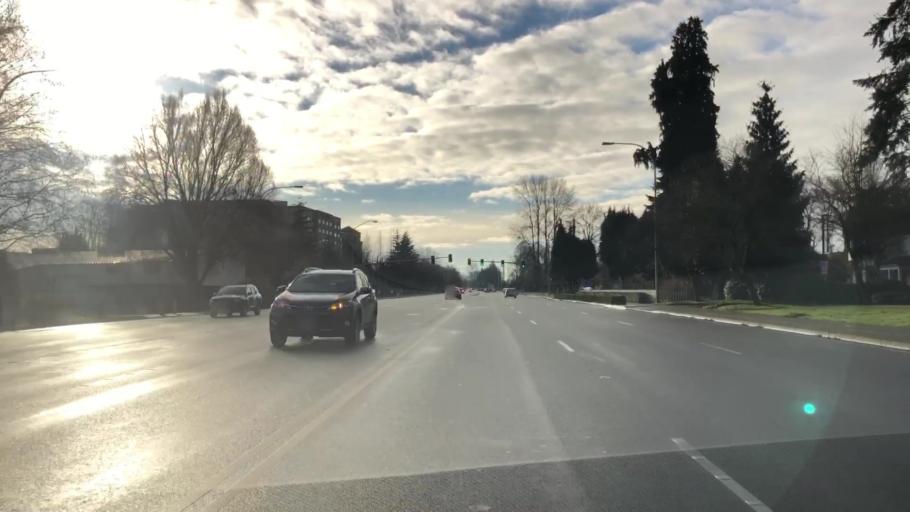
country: US
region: Washington
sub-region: King County
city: Tukwila
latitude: 47.4624
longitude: -122.2453
